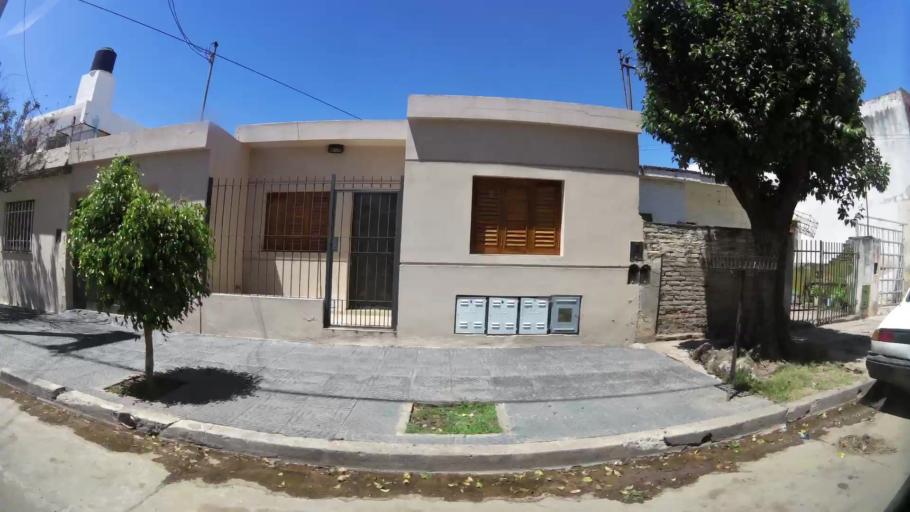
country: AR
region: Cordoba
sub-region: Departamento de Capital
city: Cordoba
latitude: -31.4364
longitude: -64.1265
